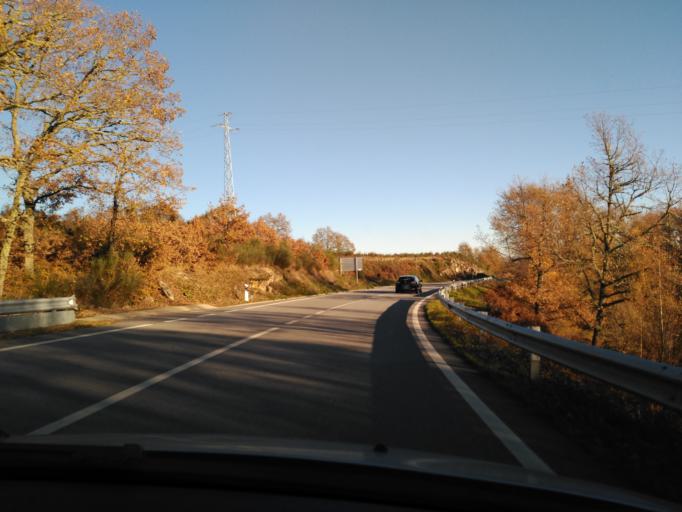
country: PT
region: Vila Real
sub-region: Montalegre
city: Montalegre
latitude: 41.7801
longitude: -7.7939
